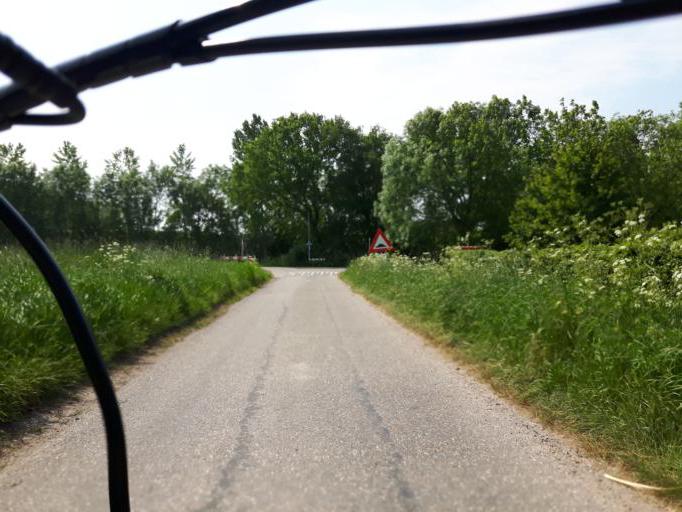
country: NL
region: North Brabant
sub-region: Gemeente Steenbergen
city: Welberg
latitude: 51.5681
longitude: 4.3421
